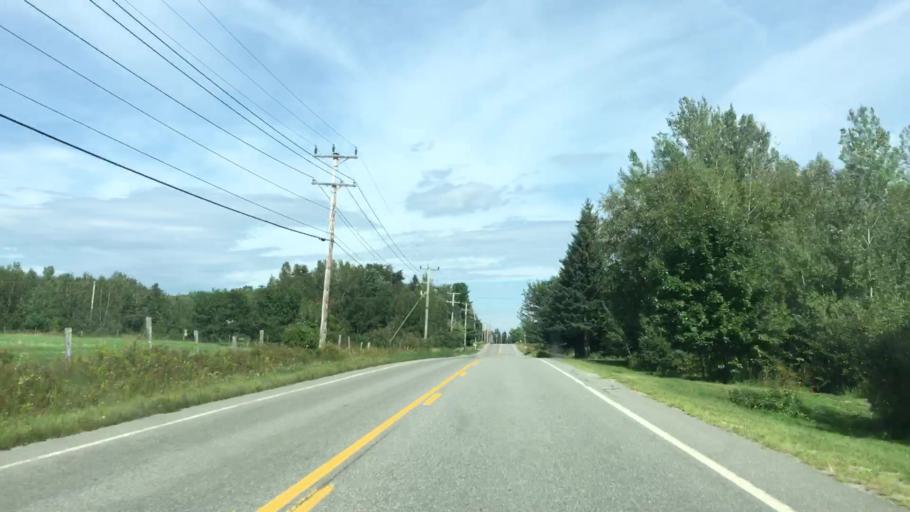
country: US
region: Maine
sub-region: Penobscot County
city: Lincoln
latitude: 45.4224
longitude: -68.4862
